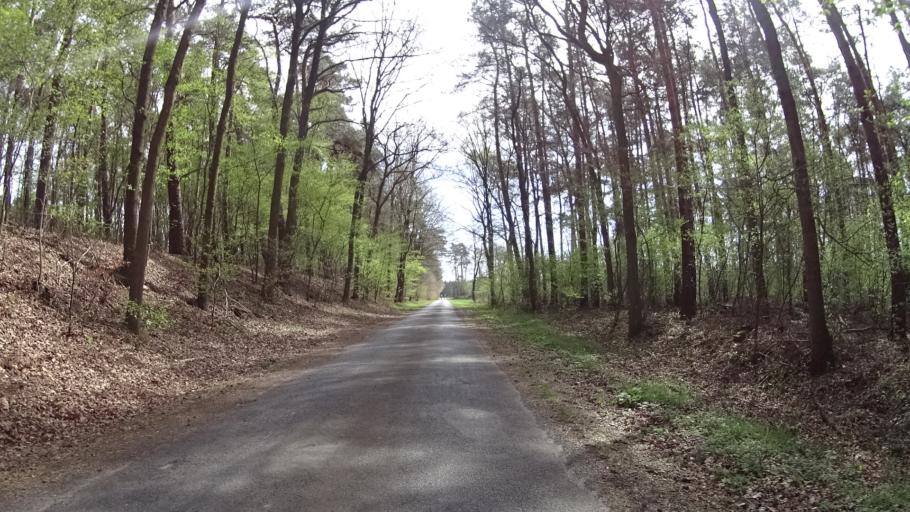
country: DE
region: Lower Saxony
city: Lunne
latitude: 52.3859
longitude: 7.3933
